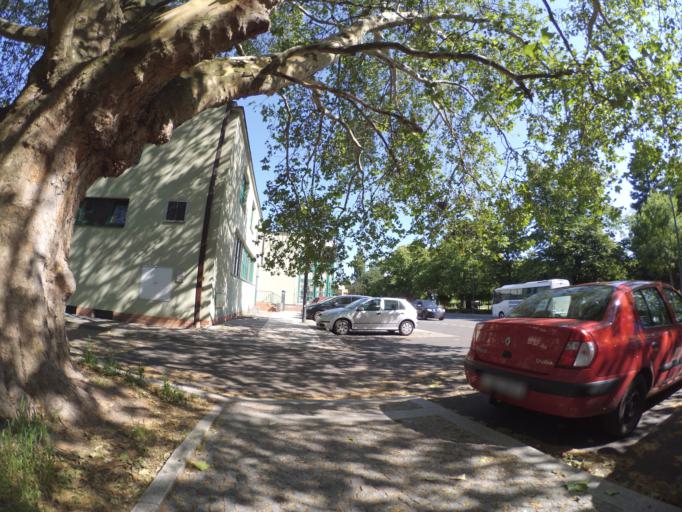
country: CZ
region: Central Bohemia
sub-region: Okres Nymburk
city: Podebrady
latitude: 50.1498
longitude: 15.1224
